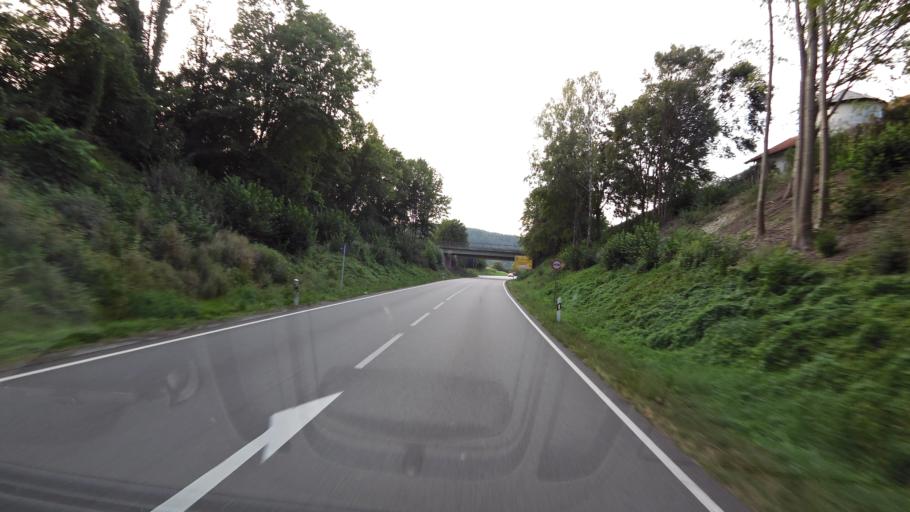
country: DE
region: Bavaria
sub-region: Lower Bavaria
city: Kirchdorf am Inn
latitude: 48.2557
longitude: 12.9988
